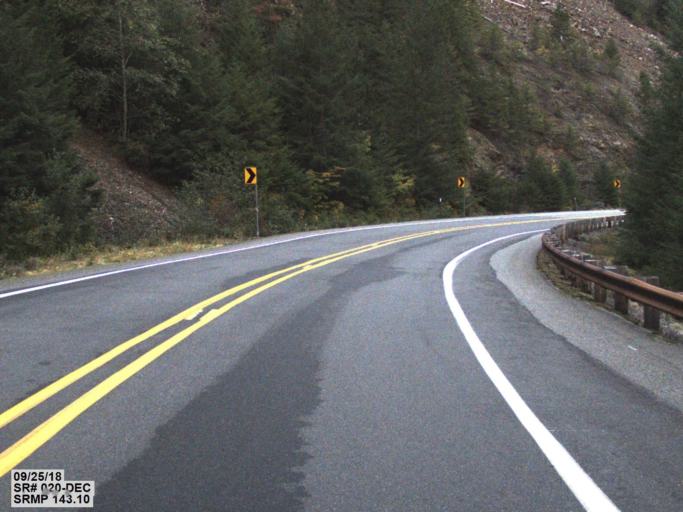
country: US
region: Washington
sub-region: Snohomish County
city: Darrington
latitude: 48.6886
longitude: -120.8891
